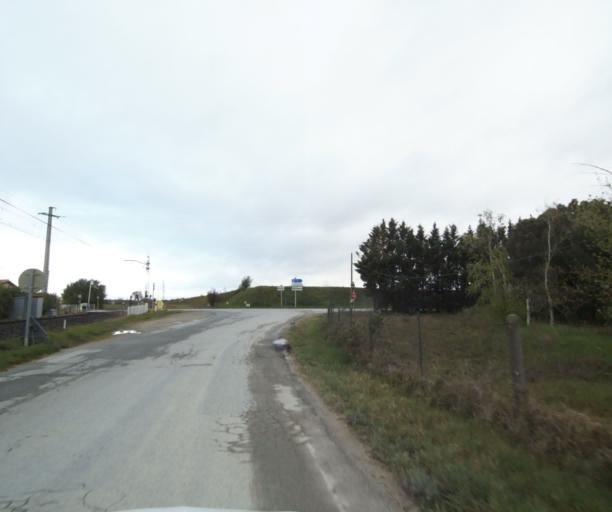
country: FR
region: Midi-Pyrenees
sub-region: Departement de l'Ariege
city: Saverdun
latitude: 43.2278
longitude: 1.6084
